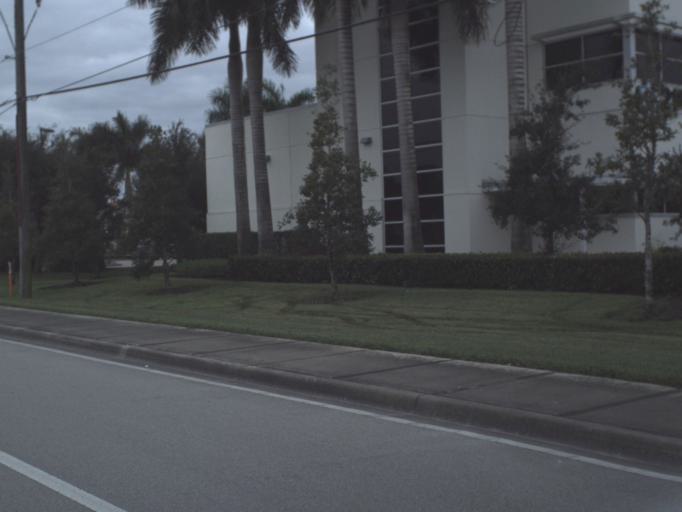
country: US
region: Florida
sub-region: Collier County
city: Lely Resort
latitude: 26.1052
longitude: -81.6873
